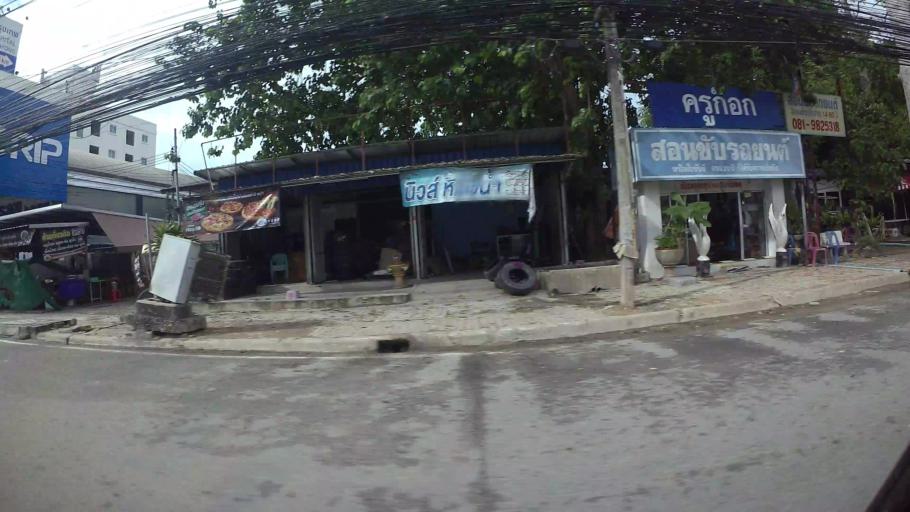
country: TH
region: Rayong
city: Rayong
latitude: 12.6832
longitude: 101.2380
